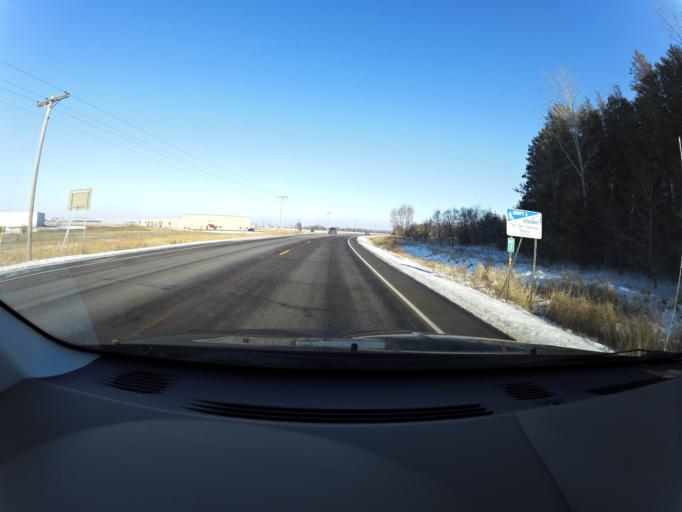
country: US
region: Minnesota
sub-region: Goodhue County
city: Cannon Falls
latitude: 44.5341
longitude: -92.9092
